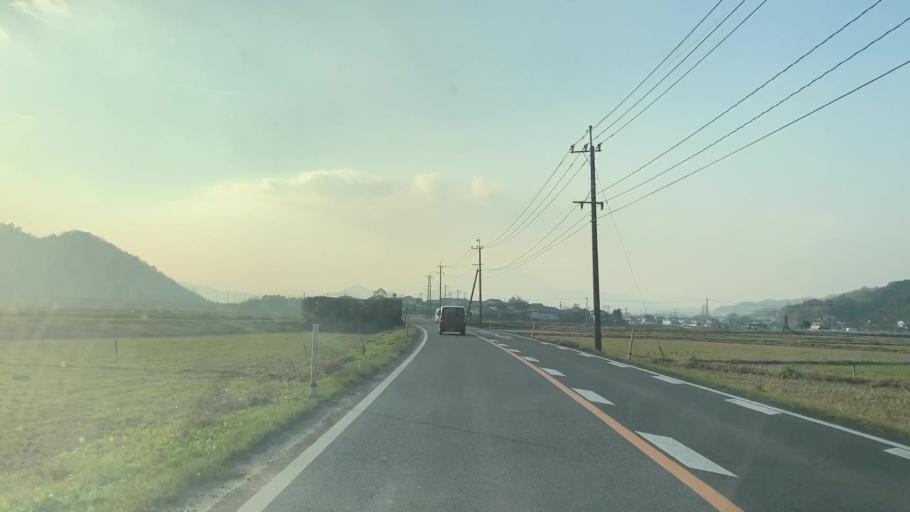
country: JP
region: Saga Prefecture
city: Saga-shi
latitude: 33.2797
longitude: 130.1634
